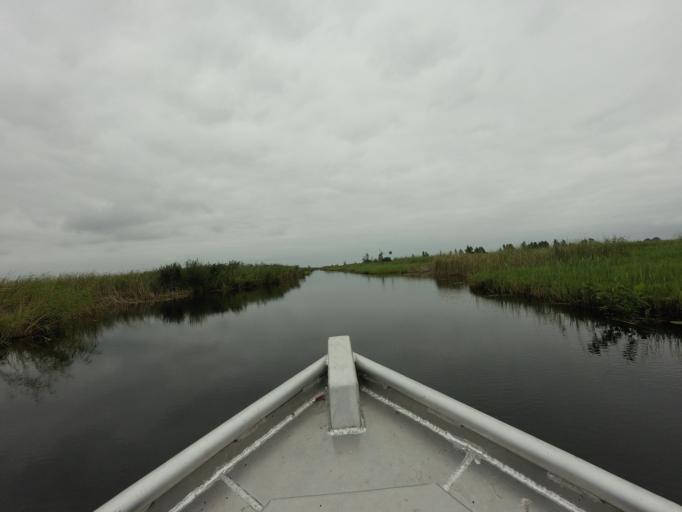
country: NL
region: Overijssel
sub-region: Gemeente Steenwijkerland
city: Blokzijl
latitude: 52.7686
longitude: 5.9259
